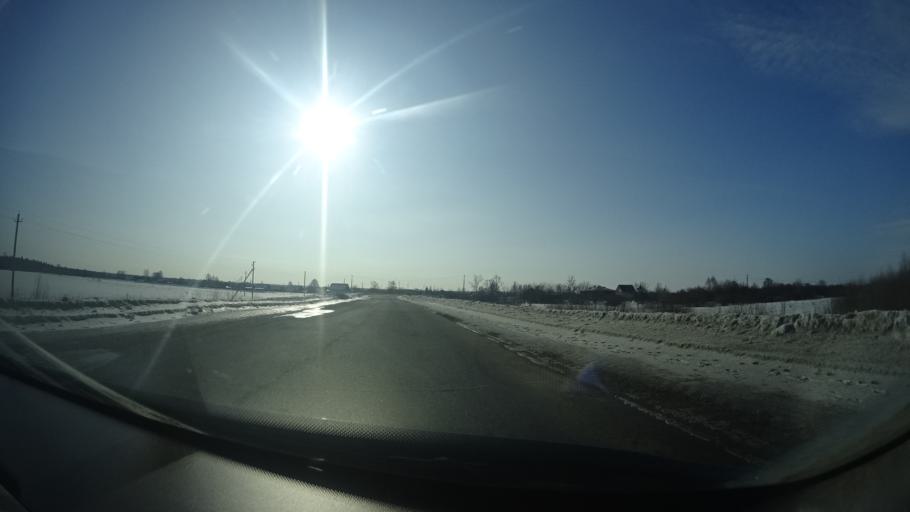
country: RU
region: Perm
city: Kuyeda
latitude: 56.4601
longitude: 55.5968
